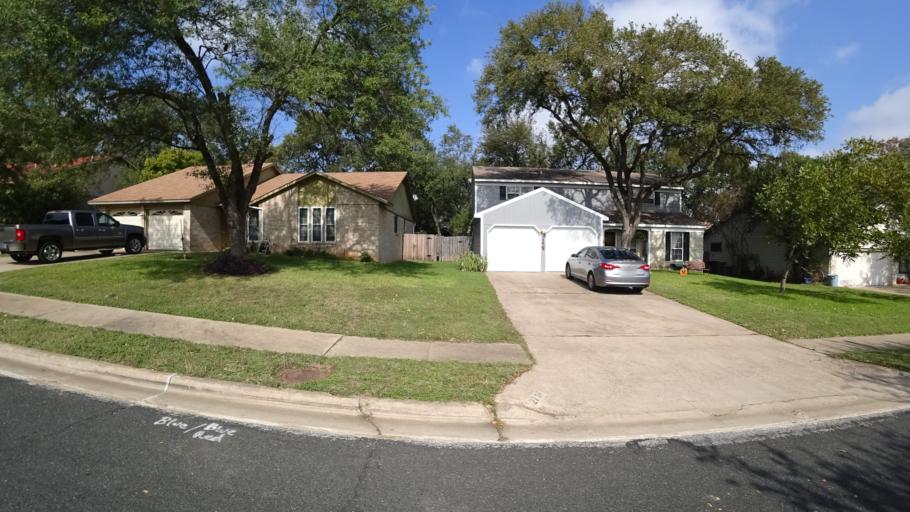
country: US
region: Texas
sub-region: Travis County
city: Shady Hollow
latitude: 30.2018
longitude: -97.8214
